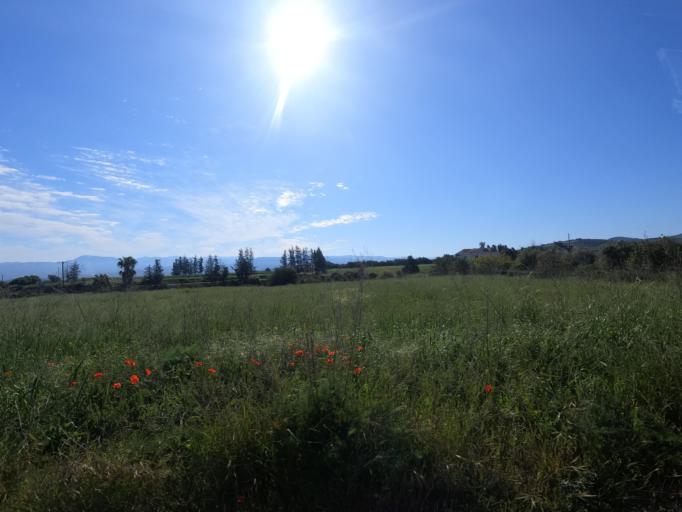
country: CY
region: Pafos
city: Polis
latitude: 35.0303
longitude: 32.3934
